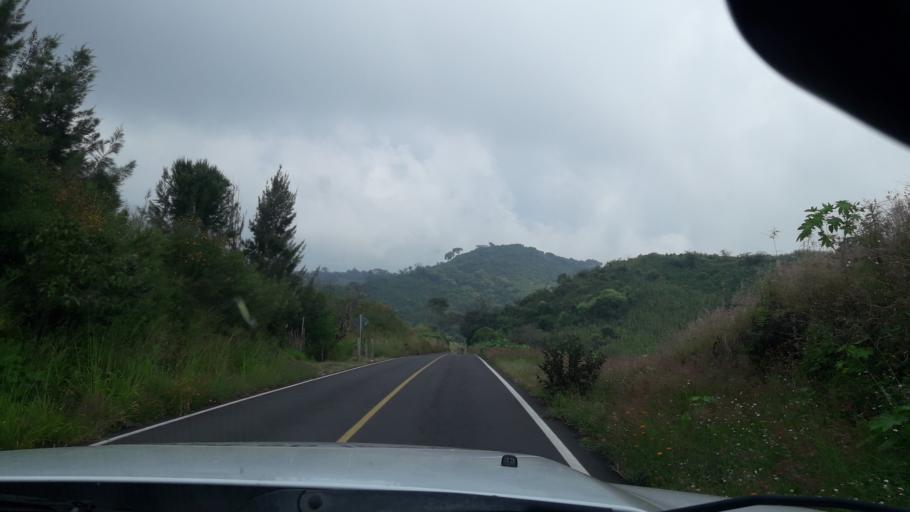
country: MX
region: Colima
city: Suchitlan
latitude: 19.4118
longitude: -103.6521
